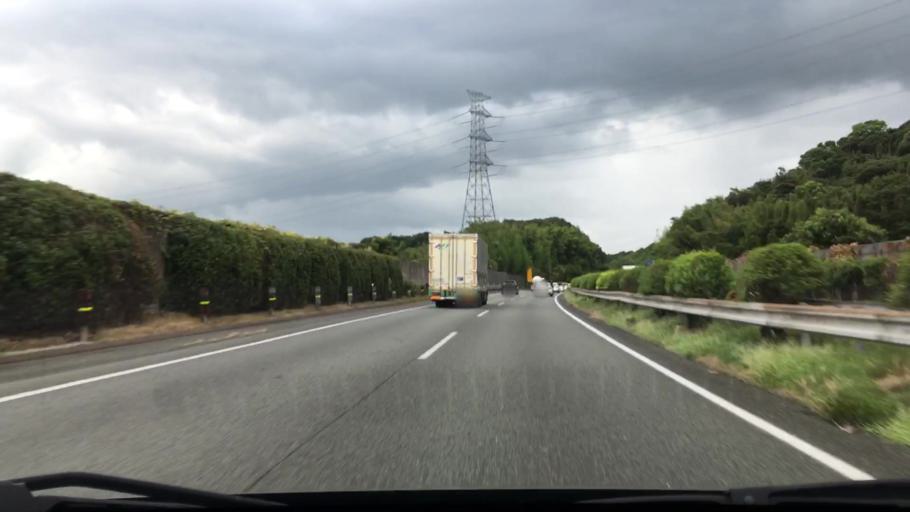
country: JP
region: Fukuoka
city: Miyata
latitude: 33.7492
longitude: 130.5904
